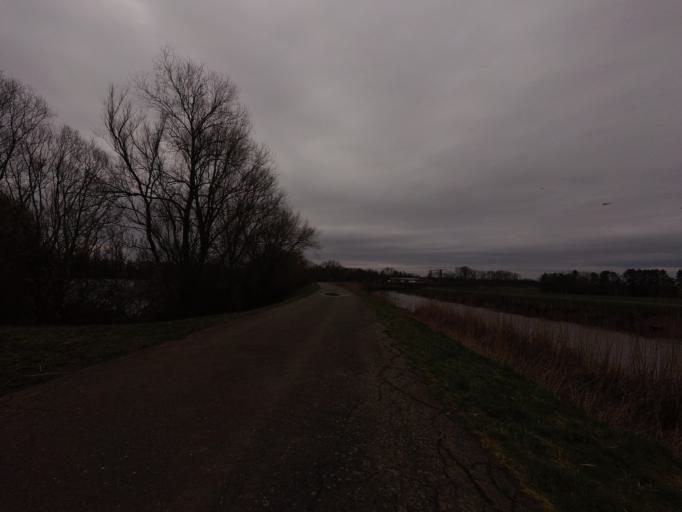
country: BE
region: Flanders
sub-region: Provincie Antwerpen
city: Lier
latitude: 51.1210
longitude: 4.5610
